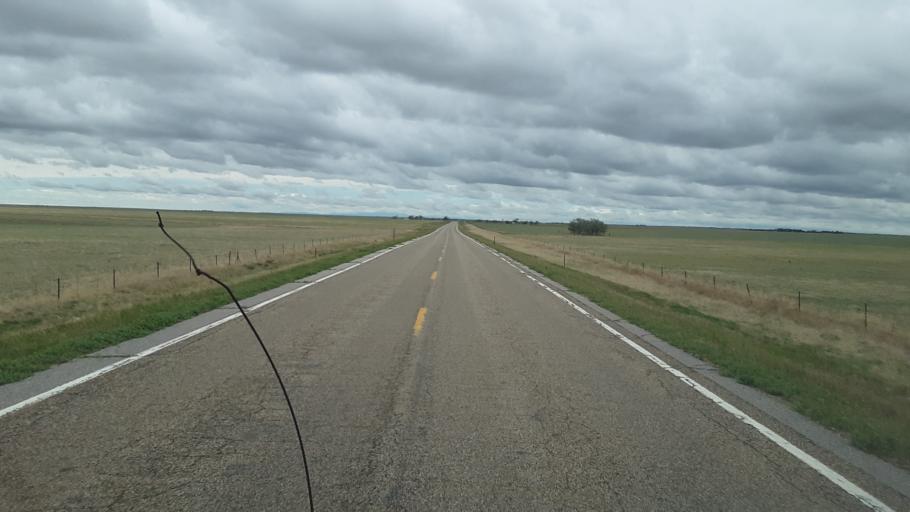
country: US
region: Colorado
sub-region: El Paso County
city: Ellicott
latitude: 38.8395
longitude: -103.9216
